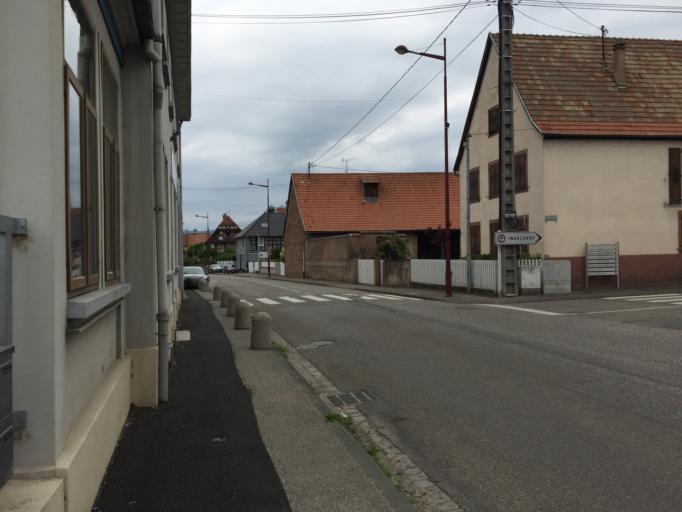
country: FR
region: Alsace
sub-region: Departement du Bas-Rhin
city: Gundershoffen
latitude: 48.9045
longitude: 7.6608
